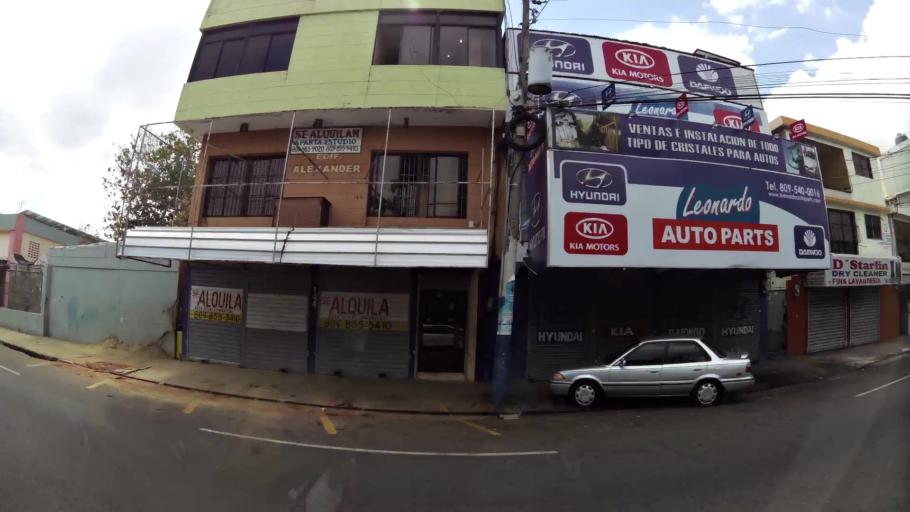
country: DO
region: Nacional
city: La Agustina
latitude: 18.4879
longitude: -69.9329
